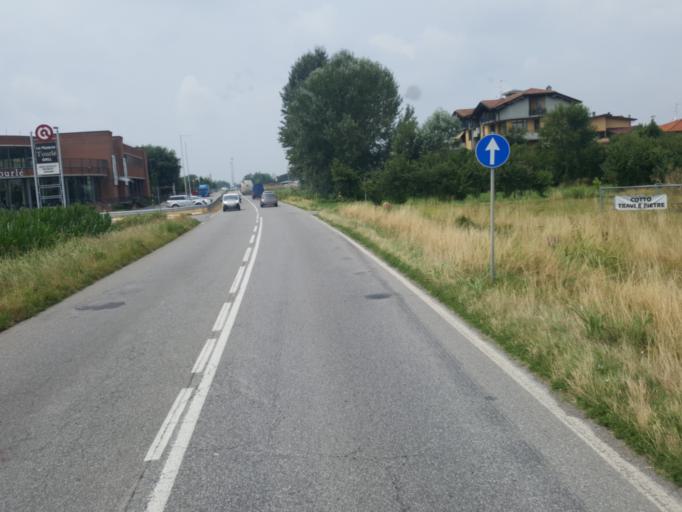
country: IT
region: Lombardy
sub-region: Provincia di Bergamo
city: Arzago d'Adda
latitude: 45.4772
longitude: 9.5648
